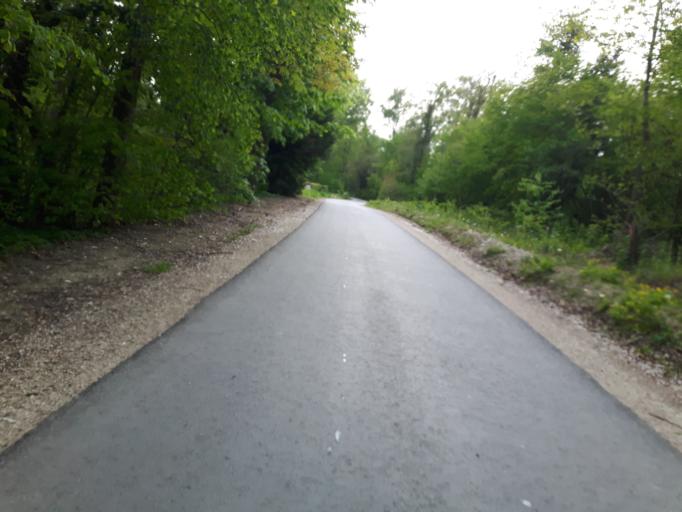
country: CH
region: Vaud
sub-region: Jura-Nord vaudois District
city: Grandson
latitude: 46.8201
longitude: 6.6705
